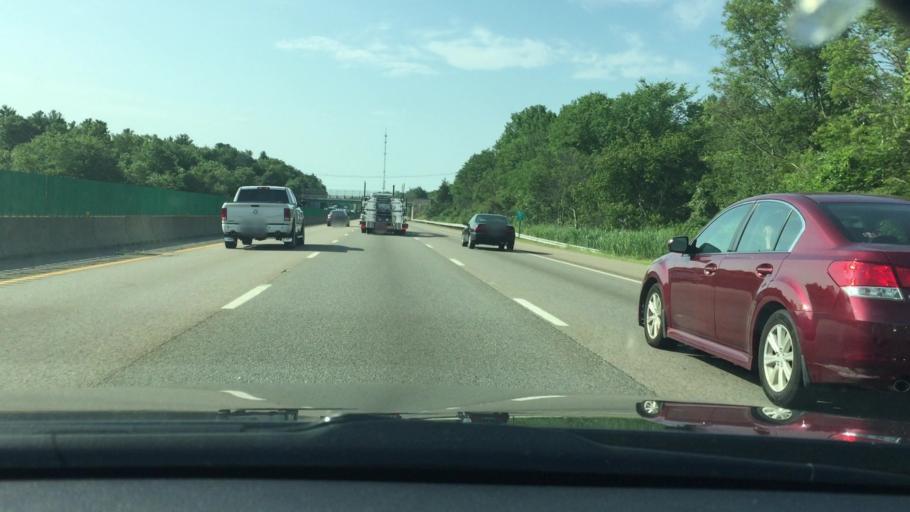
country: US
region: Massachusetts
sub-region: Plymouth County
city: West Bridgewater
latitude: 42.0256
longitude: -71.0494
